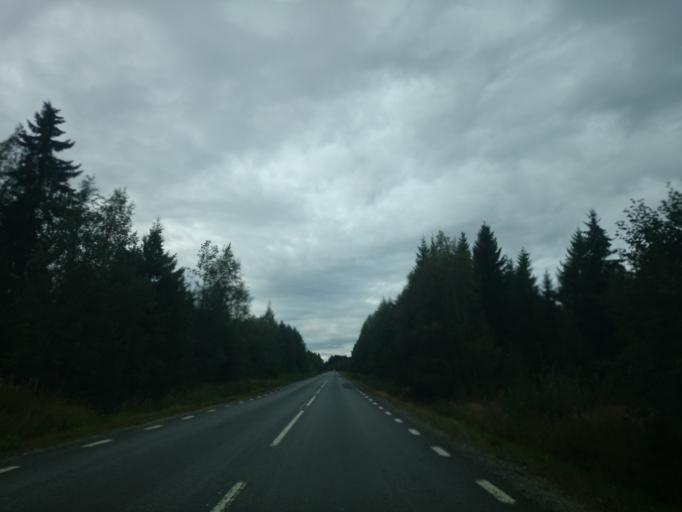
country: SE
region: Vaesternorrland
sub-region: Kramfors Kommun
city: Nordingra
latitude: 62.9994
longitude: 18.2201
